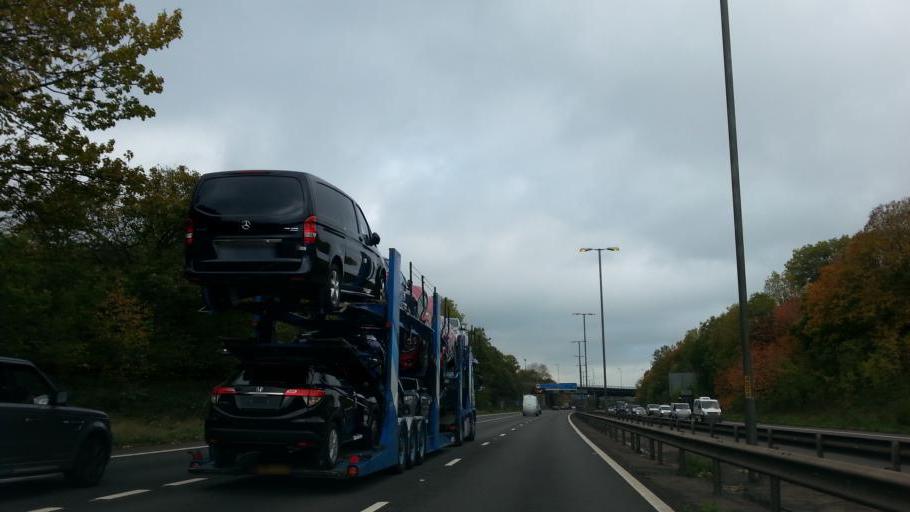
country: GB
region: England
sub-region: Sandwell
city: West Bromwich
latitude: 52.5320
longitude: -1.9707
